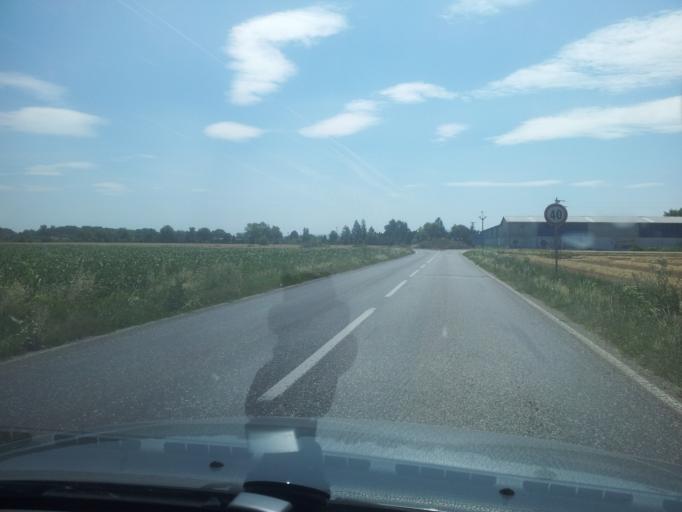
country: SK
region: Nitriansky
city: Zeliezovce
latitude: 48.1141
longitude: 18.6222
